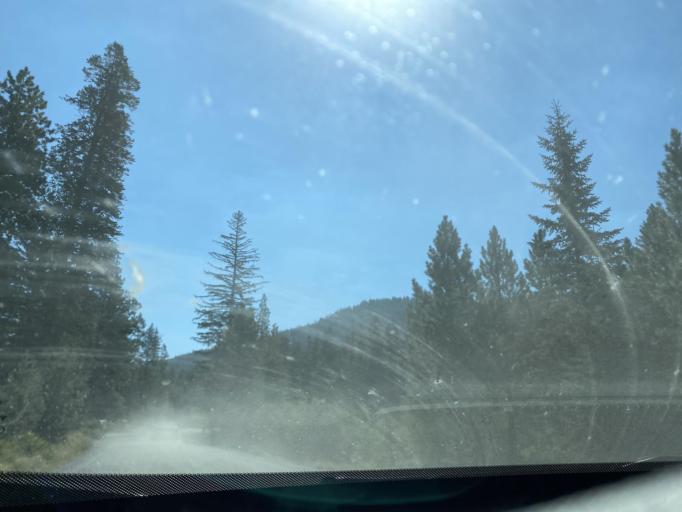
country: US
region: Oregon
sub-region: Deschutes County
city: Deschutes River Woods
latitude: 44.0325
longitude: -121.5228
